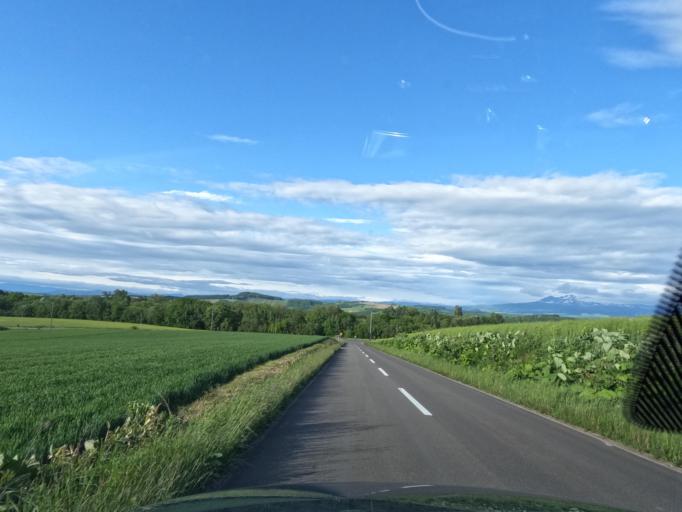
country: JP
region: Hokkaido
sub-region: Asahikawa-shi
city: Asahikawa
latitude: 43.6065
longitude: 142.4579
